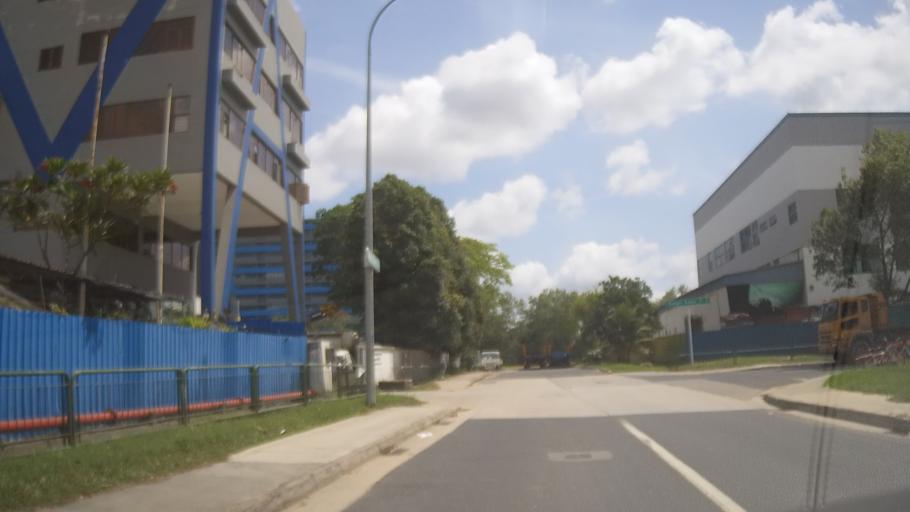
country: MY
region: Johor
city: Johor Bahru
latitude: 1.4293
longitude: 103.7502
